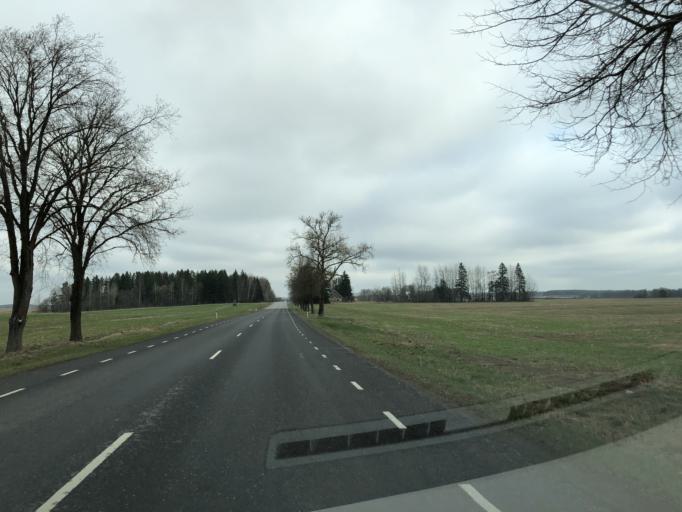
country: EE
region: Laeaene-Virumaa
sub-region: Rakvere linn
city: Rakvere
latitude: 59.2903
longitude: 26.3079
